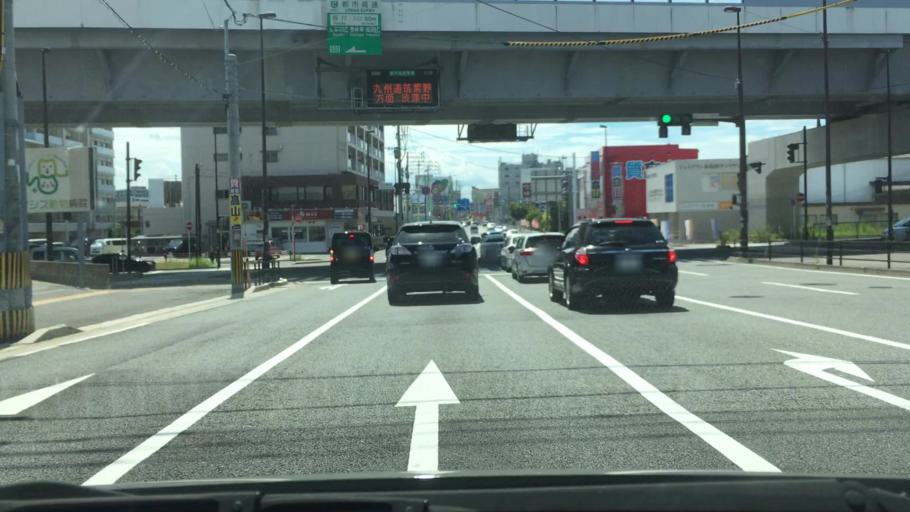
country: JP
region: Fukuoka
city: Onojo
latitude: 33.5556
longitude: 130.4535
